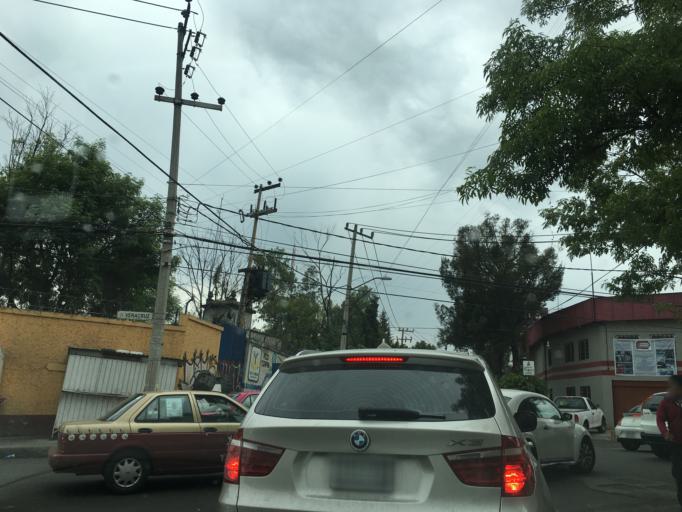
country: MX
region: Mexico City
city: Magdalena Contreras
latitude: 19.3415
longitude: -99.2014
